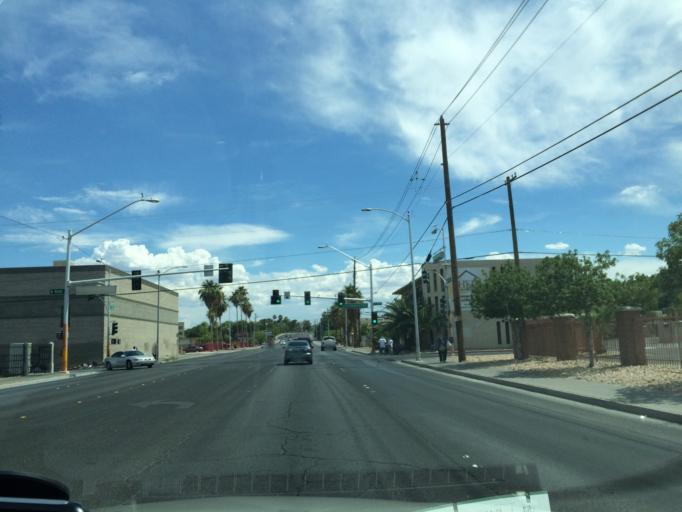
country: US
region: Nevada
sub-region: Clark County
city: Las Vegas
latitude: 36.1869
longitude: -115.1341
